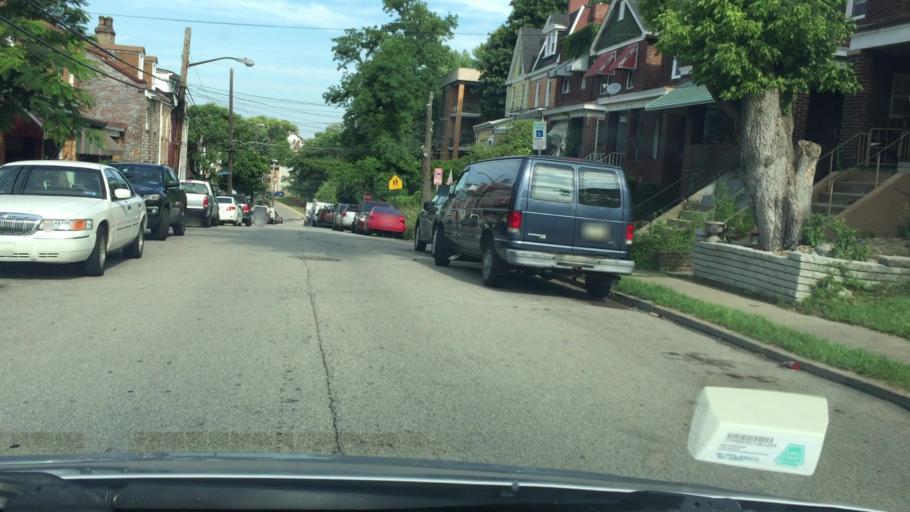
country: US
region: Pennsylvania
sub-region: Allegheny County
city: Bloomfield
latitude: 40.4522
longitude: -79.9595
